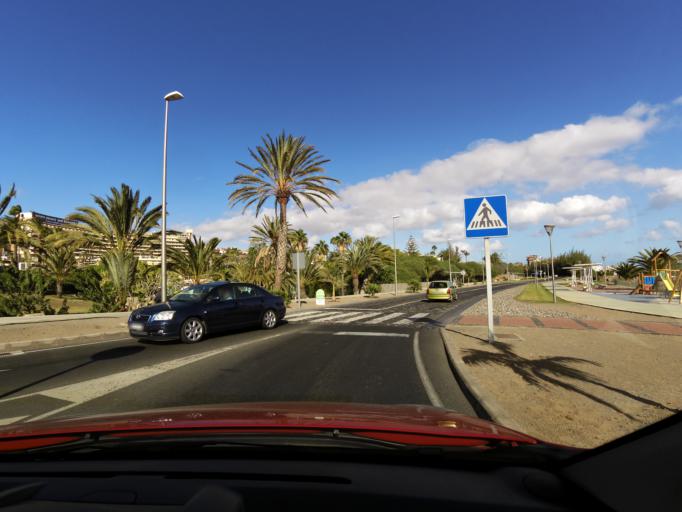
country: ES
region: Canary Islands
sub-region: Provincia de Las Palmas
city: Playa del Ingles
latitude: 27.7695
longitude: -15.5479
